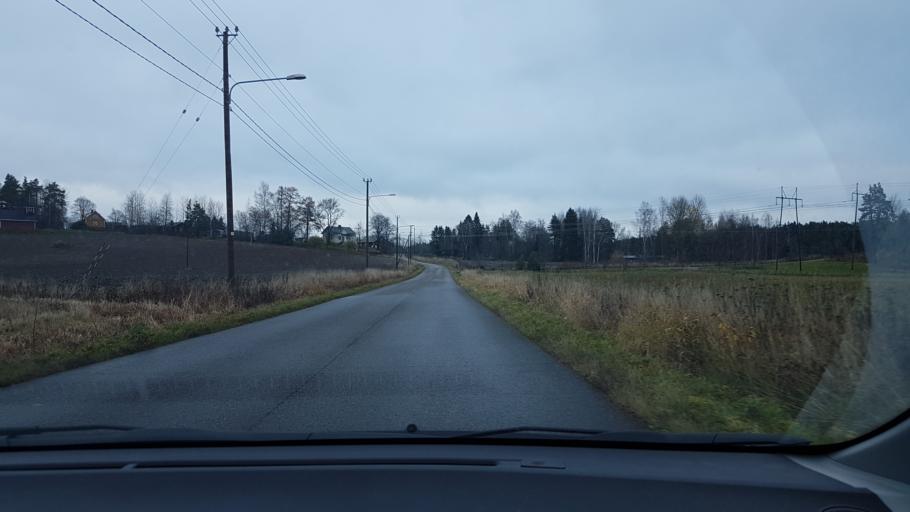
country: FI
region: Uusimaa
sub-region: Helsinki
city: Vantaa
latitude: 60.2801
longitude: 25.1373
